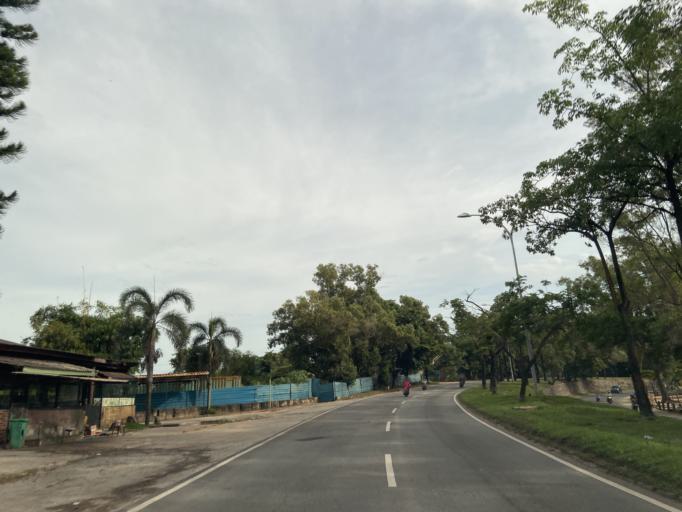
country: SG
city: Singapore
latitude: 1.1442
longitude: 104.0220
